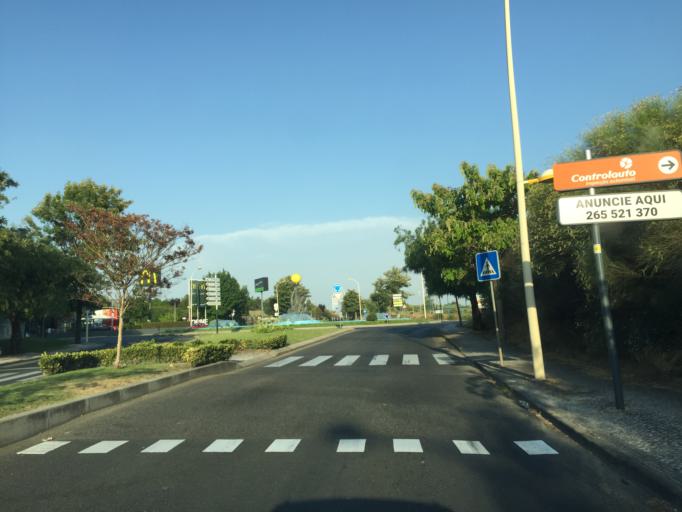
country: PT
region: Santarem
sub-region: Torres Novas
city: Torres Novas
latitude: 39.4712
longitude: -8.5414
